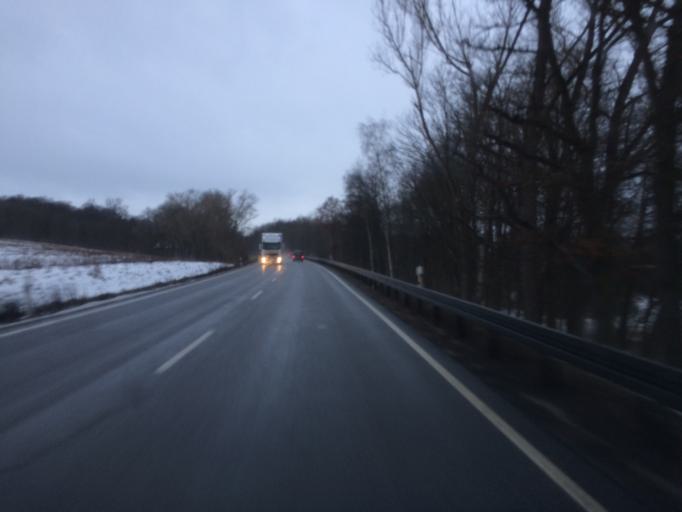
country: DE
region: Bavaria
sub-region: Upper Palatinate
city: Schwandorf in Bayern
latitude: 49.3486
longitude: 12.1326
